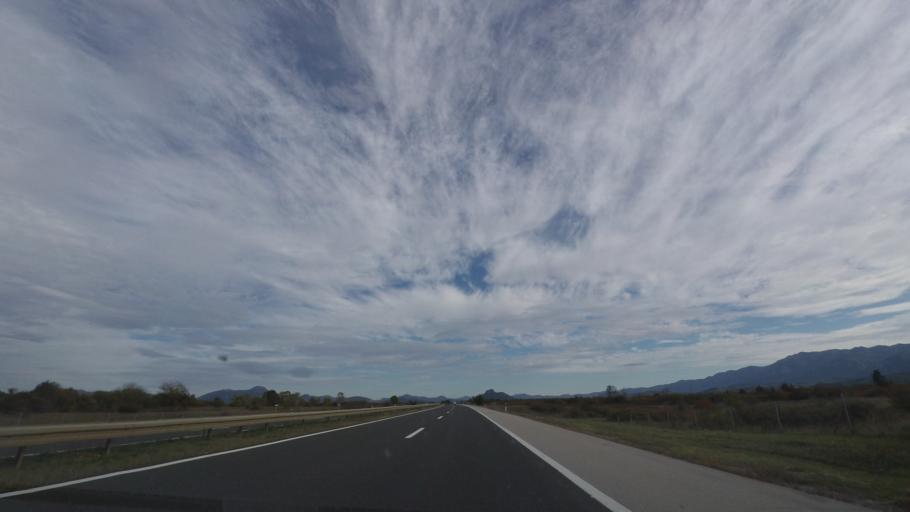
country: HR
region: Licko-Senjska
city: Gospic
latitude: 44.4889
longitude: 15.5438
